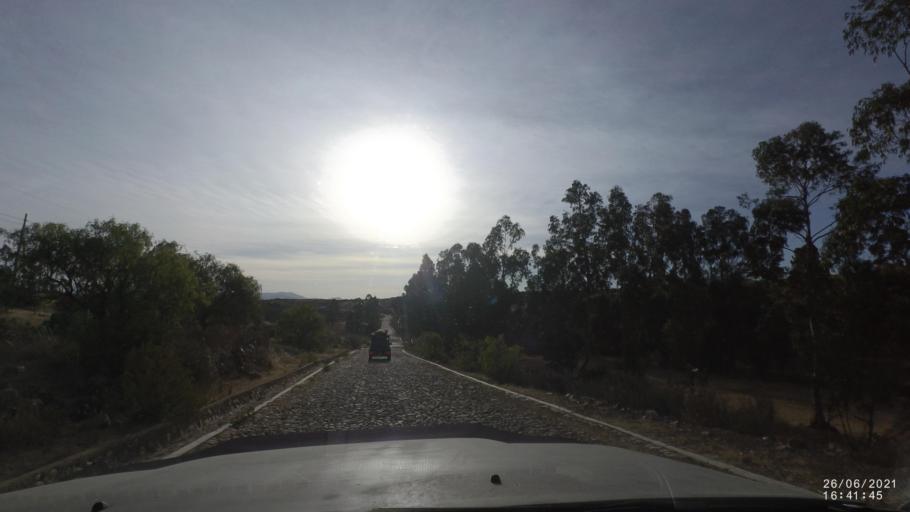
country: BO
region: Cochabamba
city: Arani
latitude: -17.7660
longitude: -65.8224
